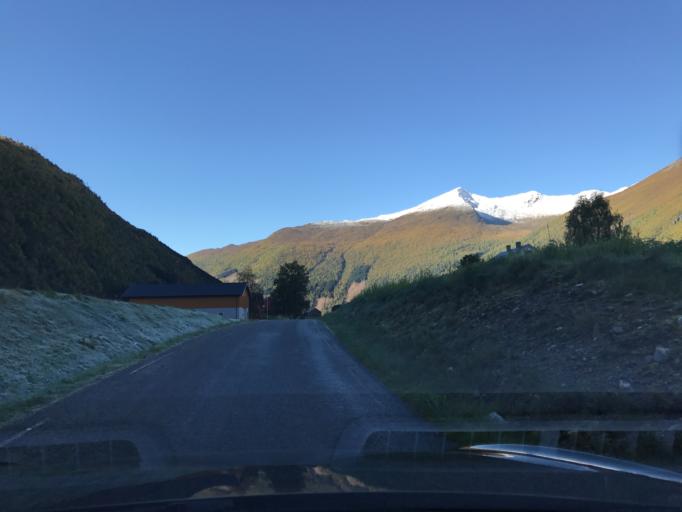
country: NO
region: More og Romsdal
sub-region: Norddal
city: Valldal
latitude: 62.3140
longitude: 7.3116
